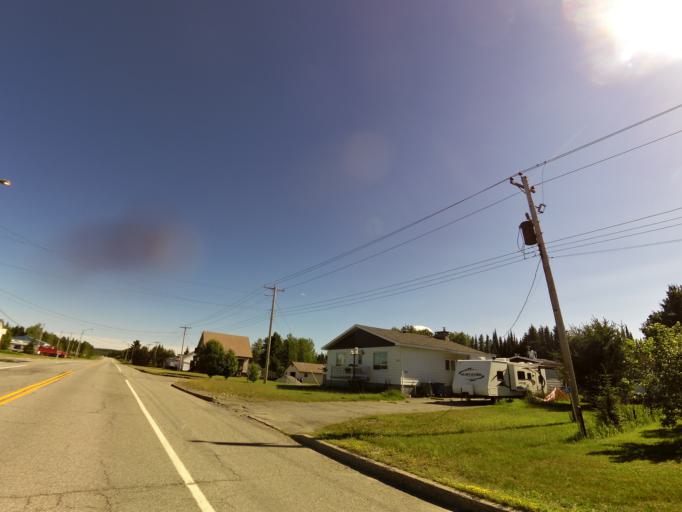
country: CA
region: Quebec
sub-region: Abitibi-Temiscamingue
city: Senneterre
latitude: 48.0688
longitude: -77.3799
